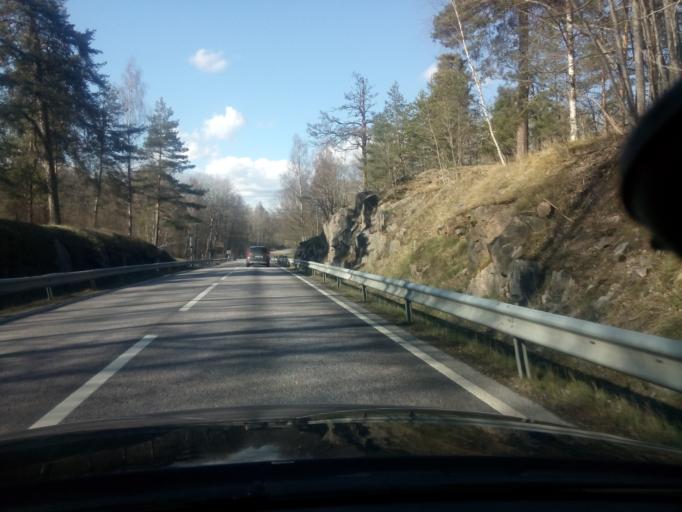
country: SE
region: Soedermanland
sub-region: Strangnas Kommun
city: Akers Styckebruk
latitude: 59.2538
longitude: 16.9407
